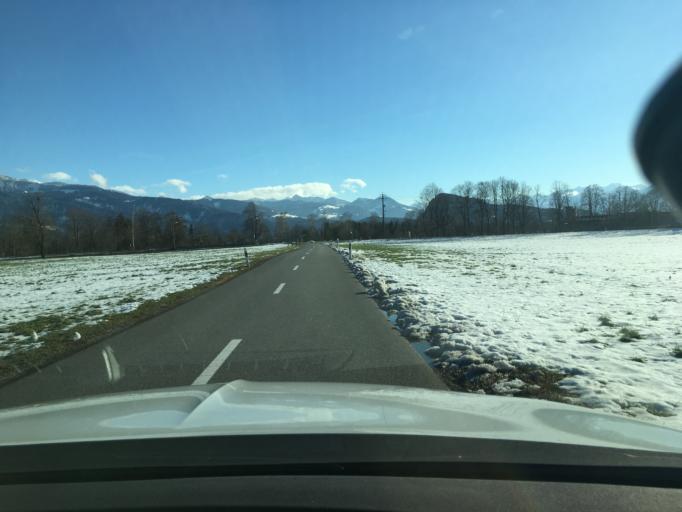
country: AT
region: Vorarlberg
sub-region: Politischer Bezirk Feldkirch
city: Mader
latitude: 47.3681
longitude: 9.5933
